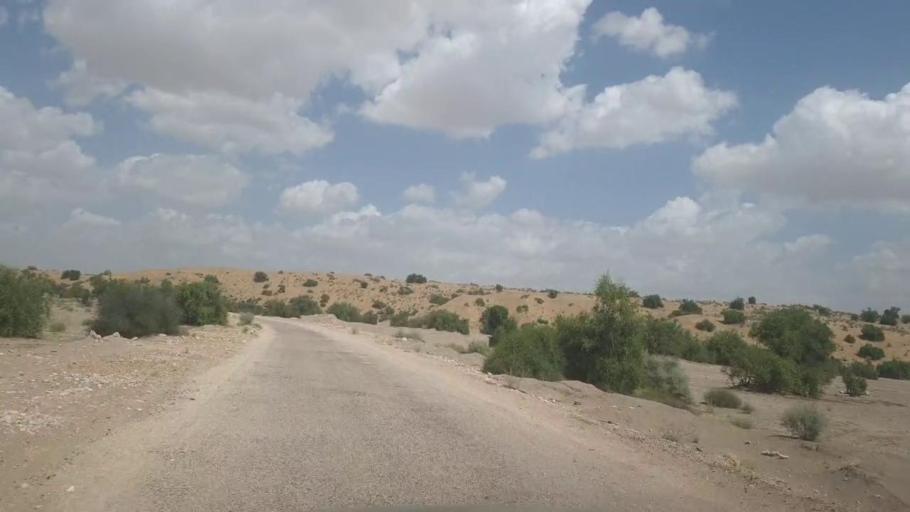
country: PK
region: Sindh
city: Kot Diji
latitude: 27.2524
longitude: 69.1599
